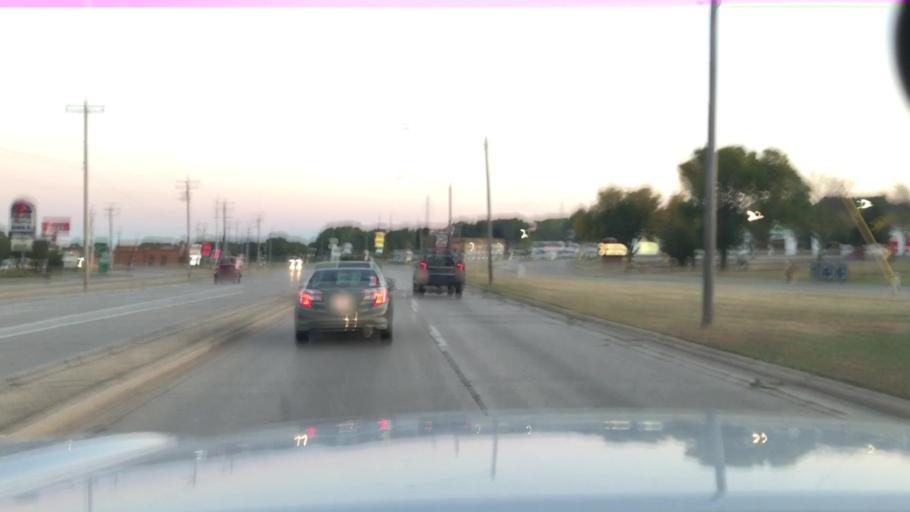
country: US
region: Wisconsin
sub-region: Brown County
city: Allouez
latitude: 44.4848
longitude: -87.9708
